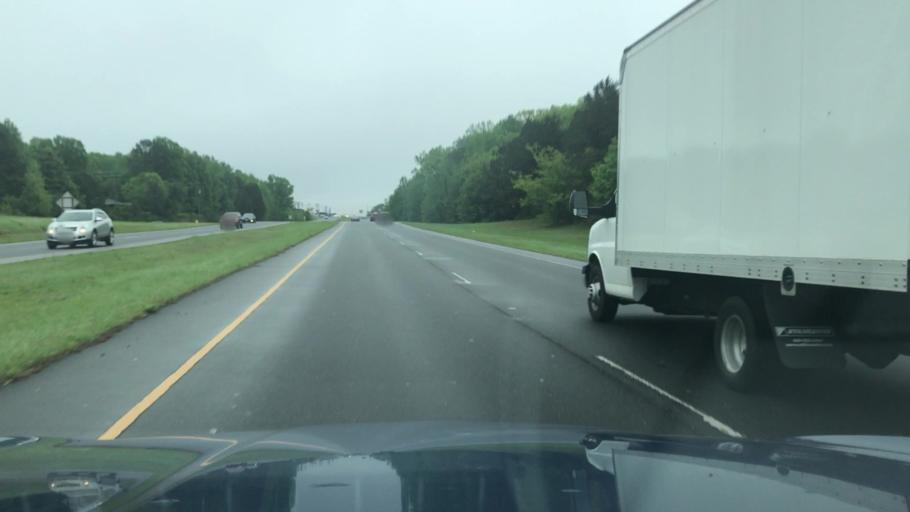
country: US
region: North Carolina
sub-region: Mecklenburg County
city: Matthews
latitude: 35.1247
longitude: -80.7042
